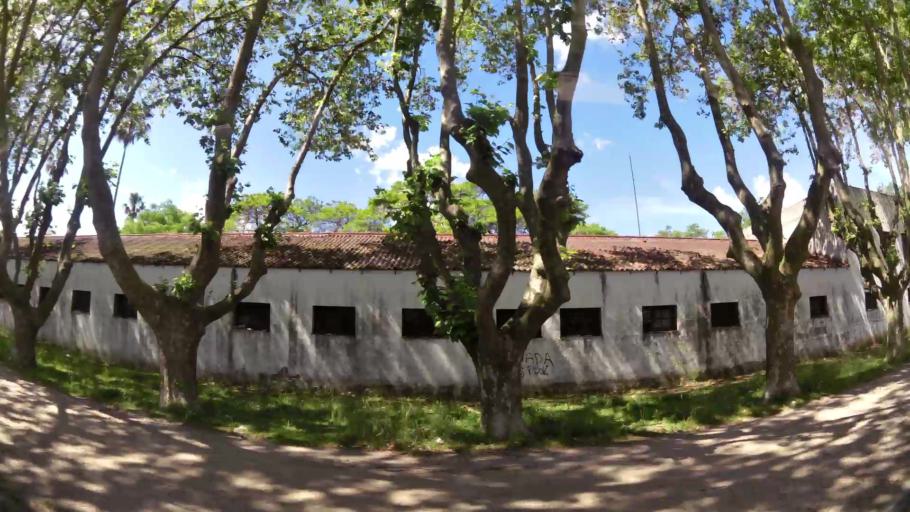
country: UY
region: Montevideo
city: Montevideo
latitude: -34.8325
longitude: -56.1397
